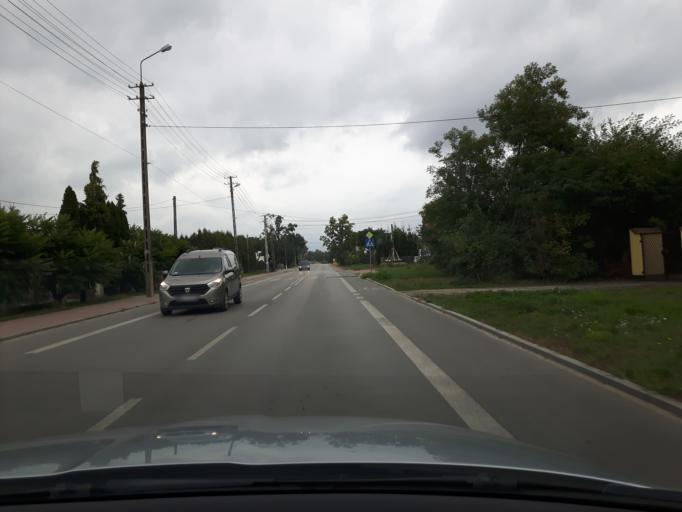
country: PL
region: Masovian Voivodeship
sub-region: Powiat wolominski
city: Kobylka
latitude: 52.3165
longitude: 21.1878
